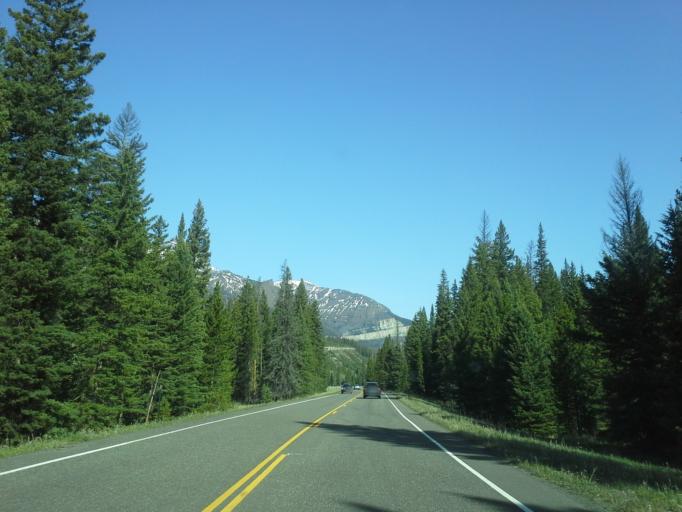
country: US
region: Montana
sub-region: Carbon County
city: Red Lodge
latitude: 44.9599
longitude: -109.8169
